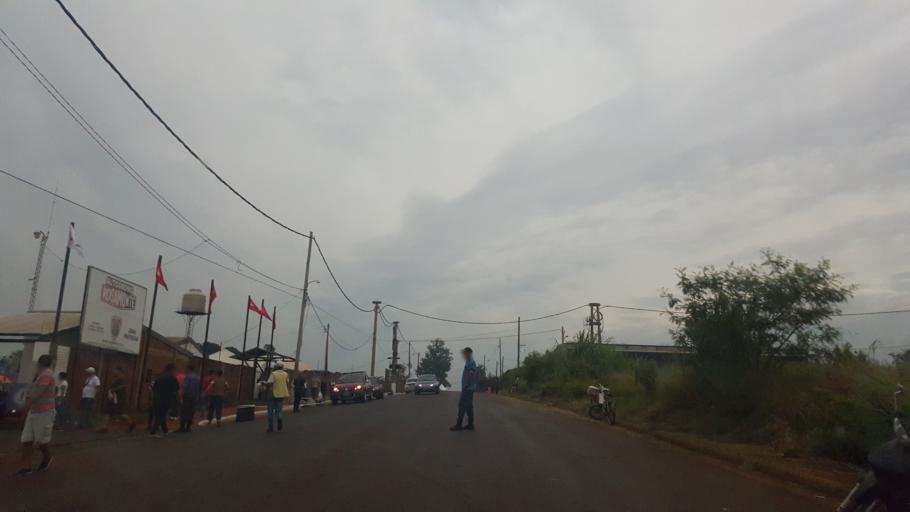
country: AR
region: Misiones
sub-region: Departamento de Capital
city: Posadas
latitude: -27.4370
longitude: -55.9229
